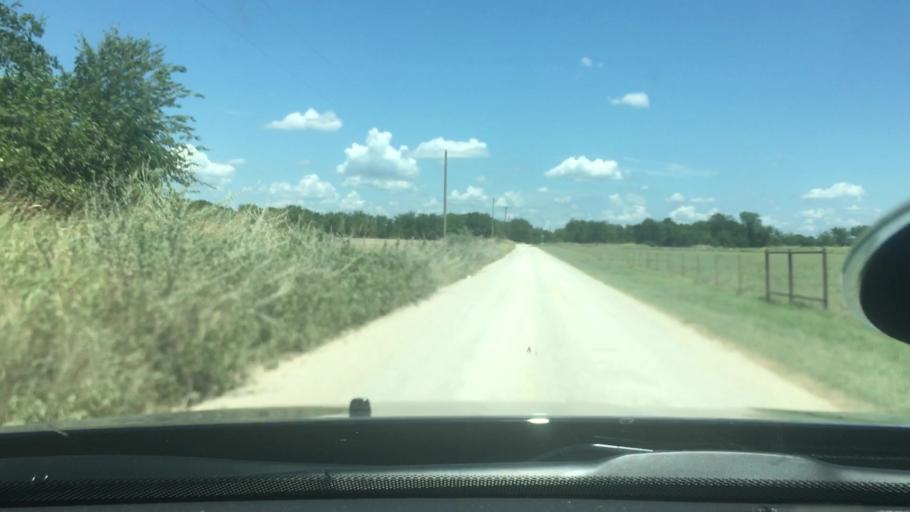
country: US
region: Oklahoma
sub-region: Bryan County
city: Durant
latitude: 34.0068
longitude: -96.1126
